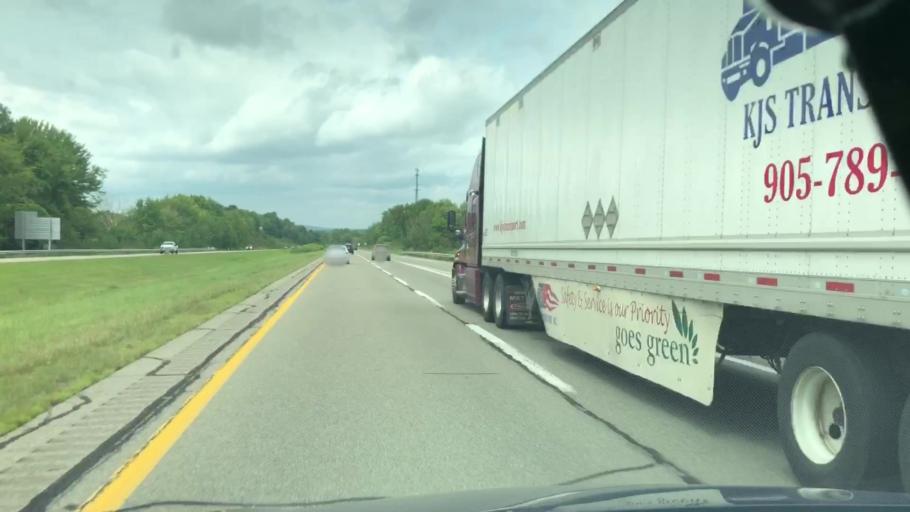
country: US
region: Pennsylvania
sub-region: Crawford County
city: Meadville
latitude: 41.7187
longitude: -80.2017
